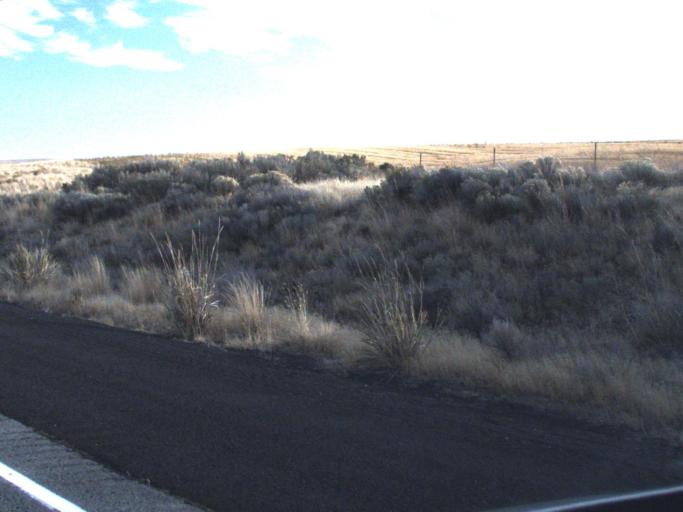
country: US
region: Washington
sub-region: Adams County
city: Ritzville
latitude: 46.9506
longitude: -118.5772
